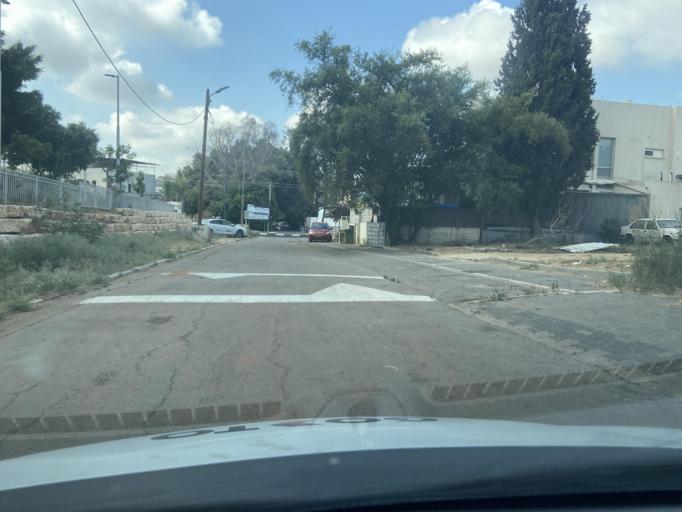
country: IL
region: Central District
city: Yehud
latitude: 32.0387
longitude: 34.8912
